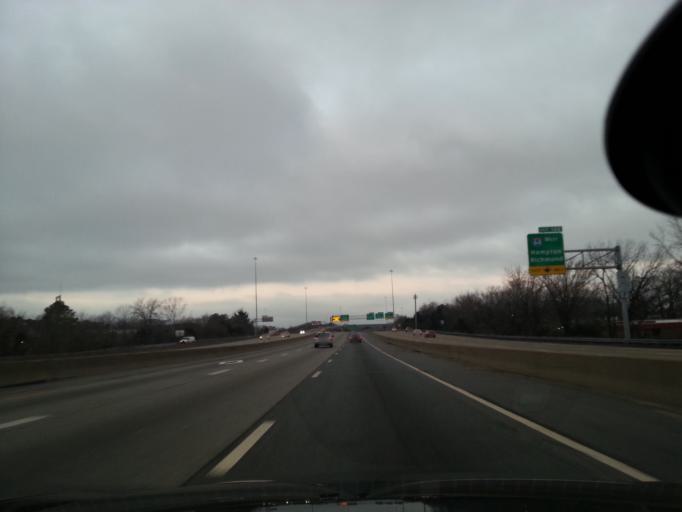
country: US
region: Virginia
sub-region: City of Chesapeake
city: Chesapeake
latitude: 36.8461
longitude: -76.1869
